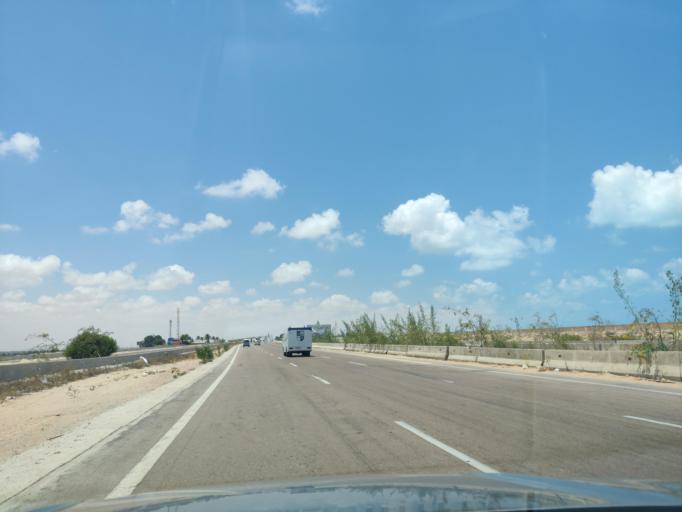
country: EG
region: Muhafazat Matruh
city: Al `Alamayn
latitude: 30.8126
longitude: 29.0728
